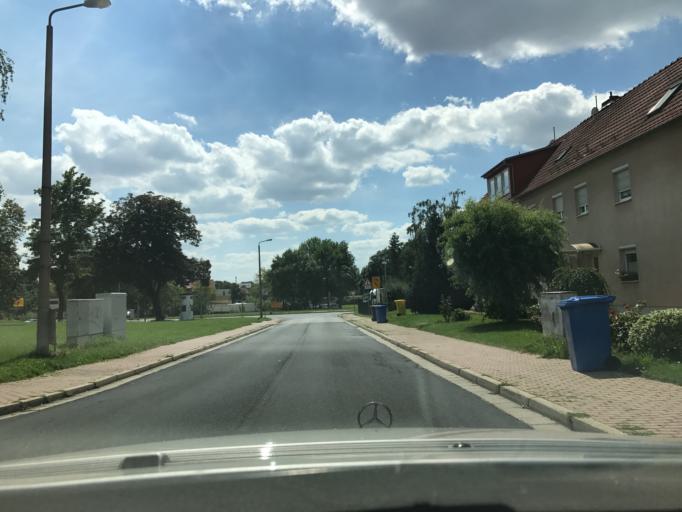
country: DE
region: Thuringia
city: Muehlhausen
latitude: 51.2162
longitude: 10.4725
